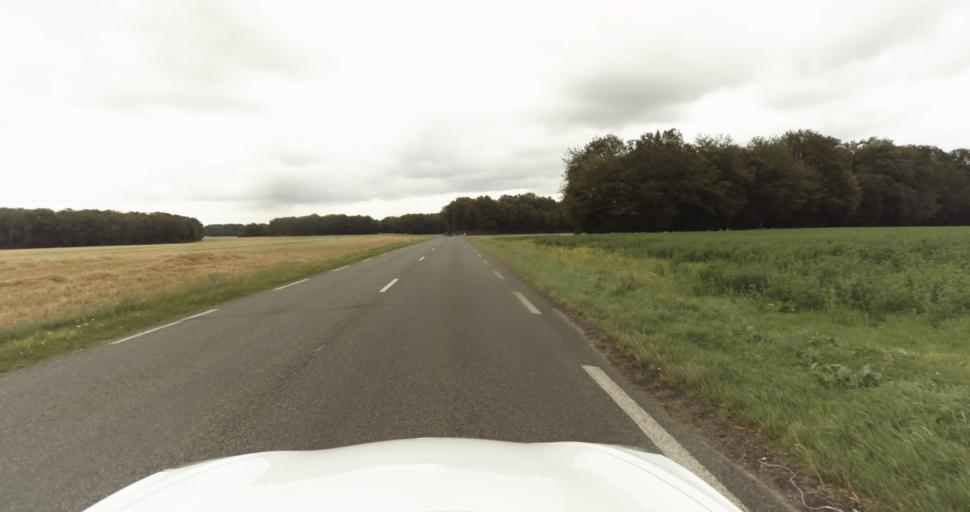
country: FR
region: Haute-Normandie
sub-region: Departement de l'Eure
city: Saint-Sebastien-de-Morsent
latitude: 49.0330
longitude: 1.0692
